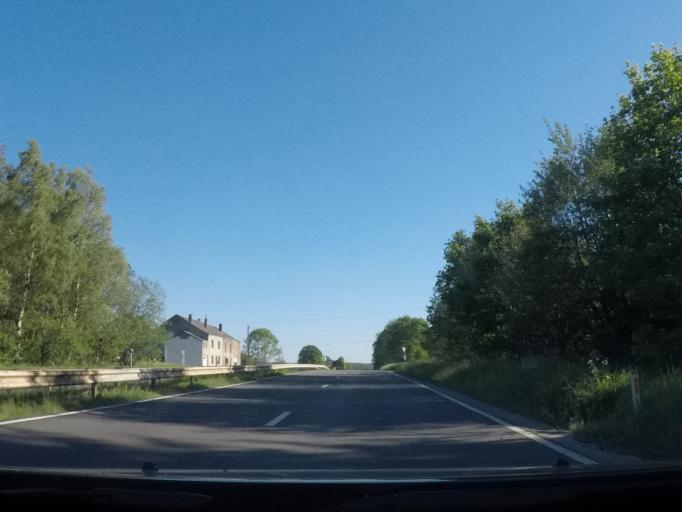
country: BE
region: Wallonia
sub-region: Province du Luxembourg
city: Saint-Hubert
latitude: 49.9993
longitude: 5.3814
